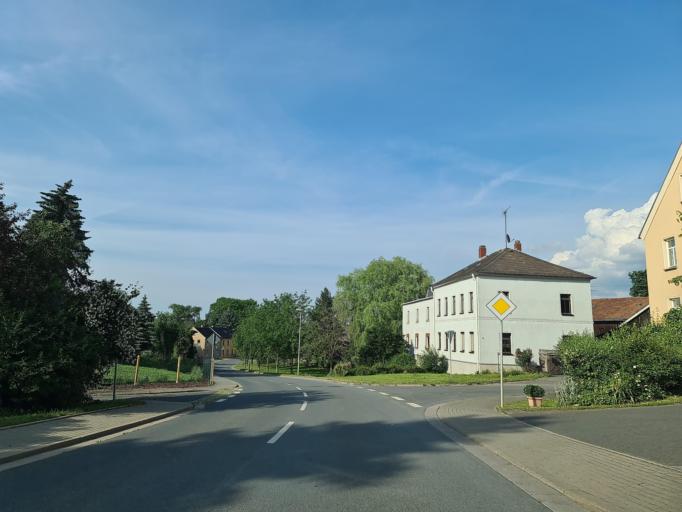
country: DE
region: Saxony
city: Bosenbrunn
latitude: 50.4060
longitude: 12.1277
